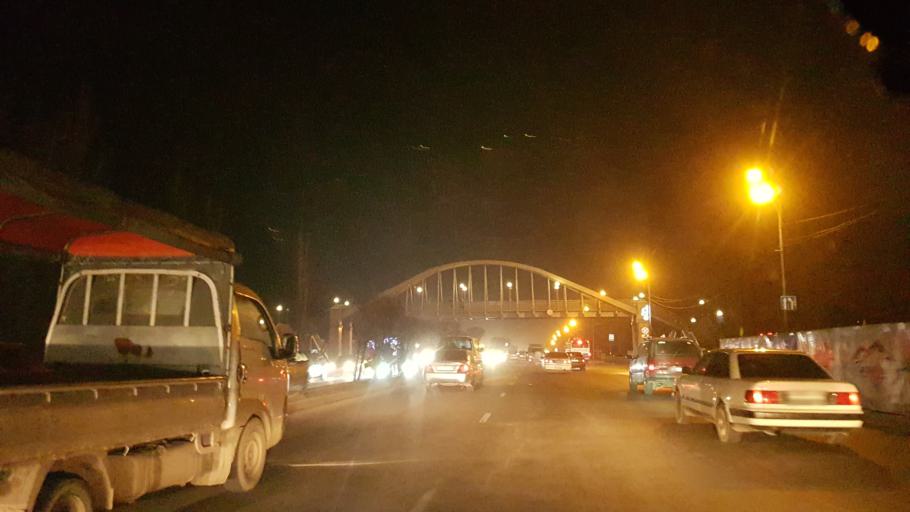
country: KZ
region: Almaty Qalasy
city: Almaty
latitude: 43.2627
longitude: 76.8592
